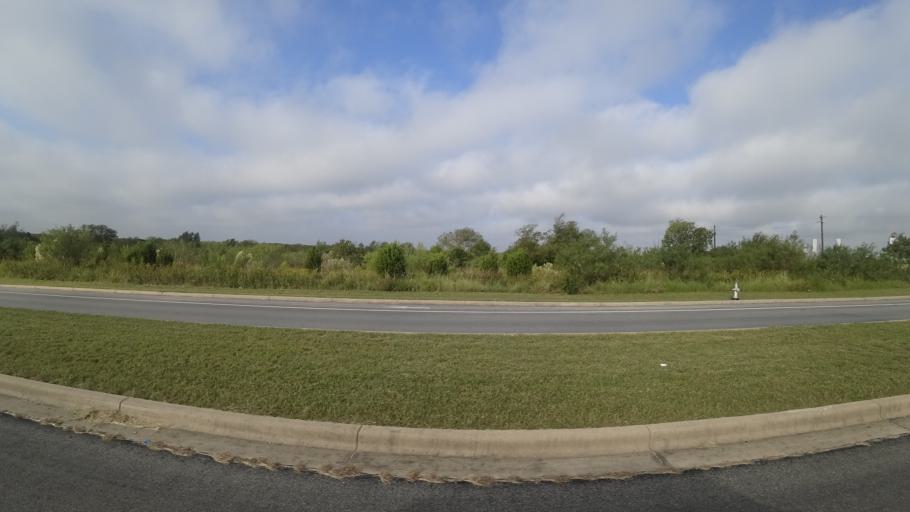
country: US
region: Texas
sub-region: Travis County
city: Pflugerville
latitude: 30.3690
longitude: -97.6353
